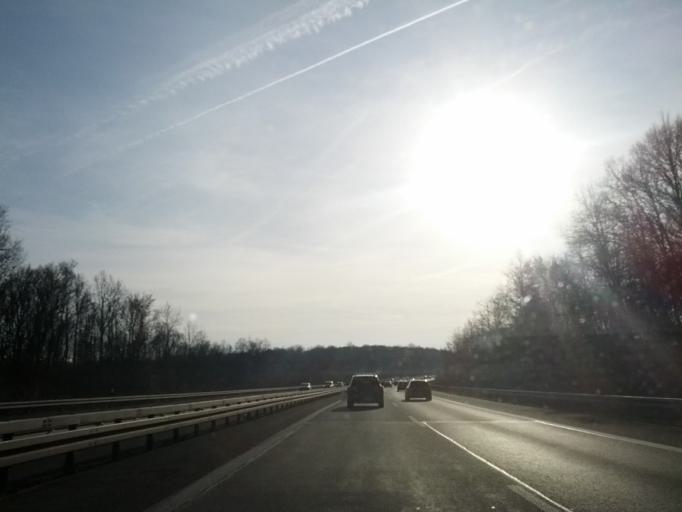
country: DE
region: Bavaria
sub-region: Regierungsbezirk Unterfranken
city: Kurnach
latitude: 49.8254
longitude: 10.0427
